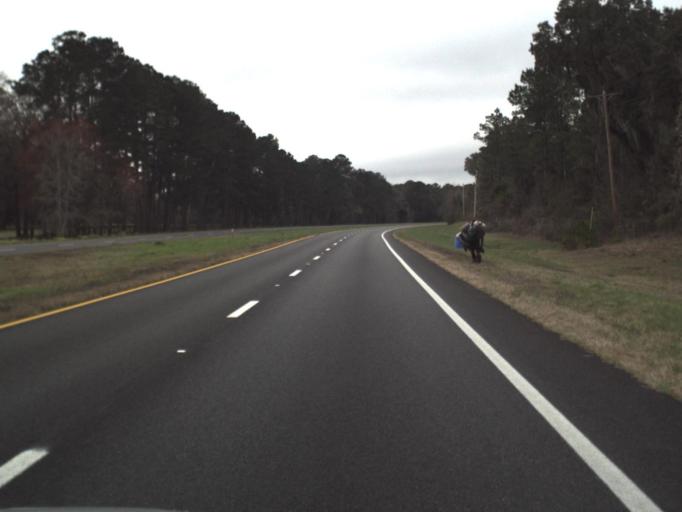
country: US
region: Florida
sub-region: Jefferson County
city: Monticello
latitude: 30.3891
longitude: -83.8571
